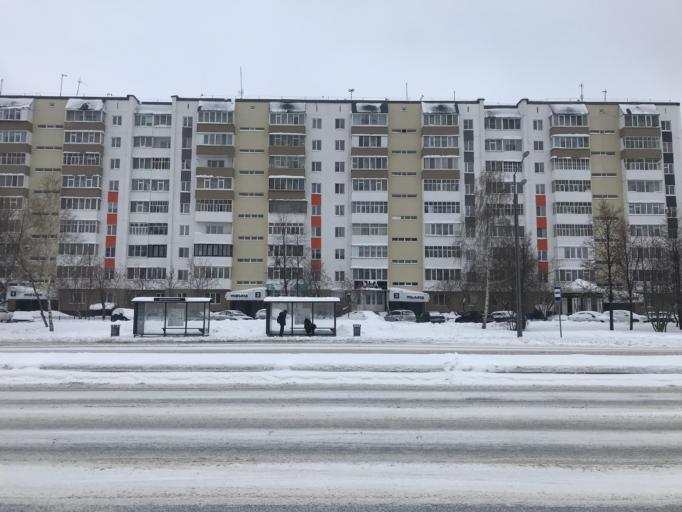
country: RU
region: Tjumen
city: Tobol'sk
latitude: 58.2281
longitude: 68.2789
